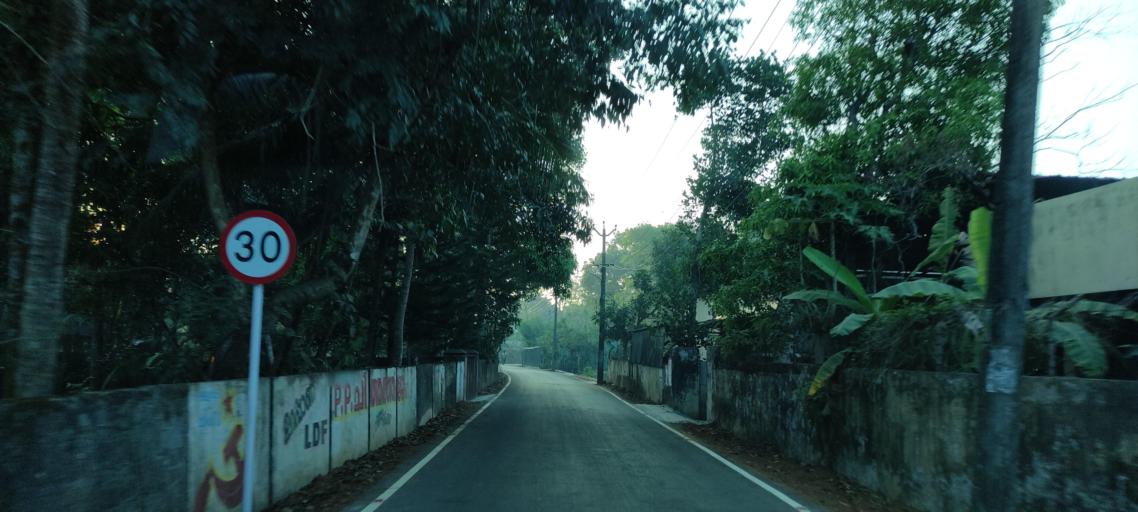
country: IN
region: Kerala
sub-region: Alappuzha
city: Alleppey
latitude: 9.5349
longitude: 76.3320
